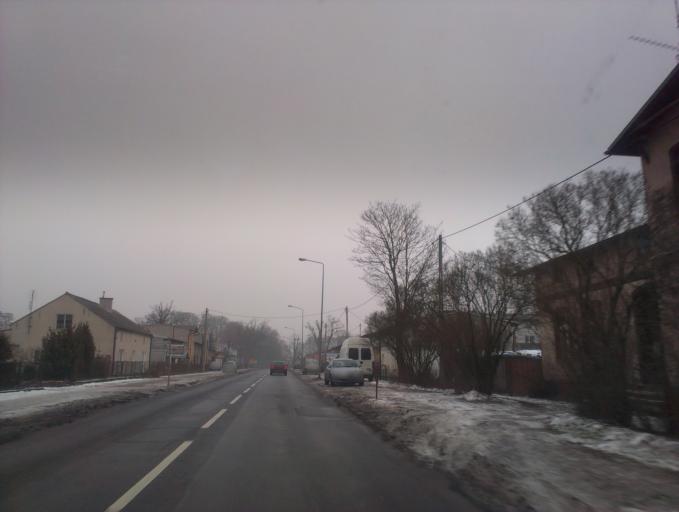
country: PL
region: Greater Poland Voivodeship
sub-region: Powiat pilski
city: Pila
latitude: 53.1708
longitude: 16.7397
